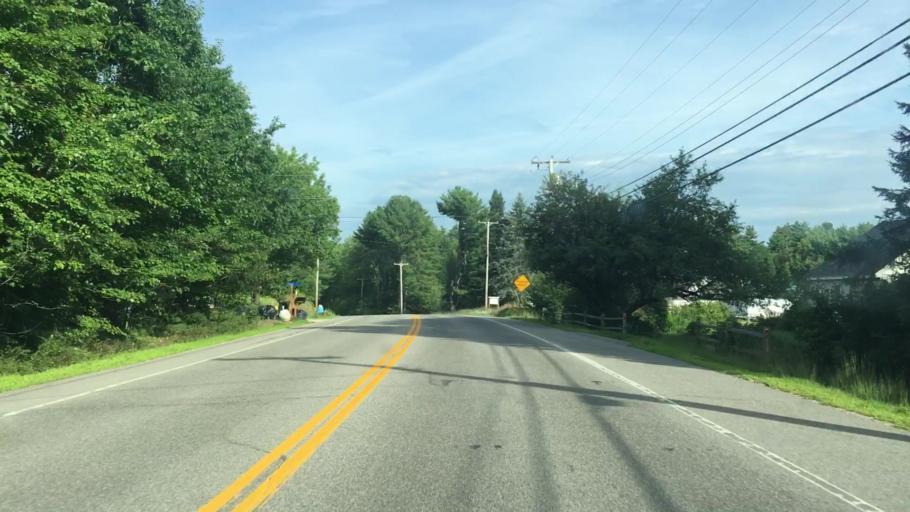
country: US
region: Maine
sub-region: York County
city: Limington
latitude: 43.7372
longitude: -70.6679
